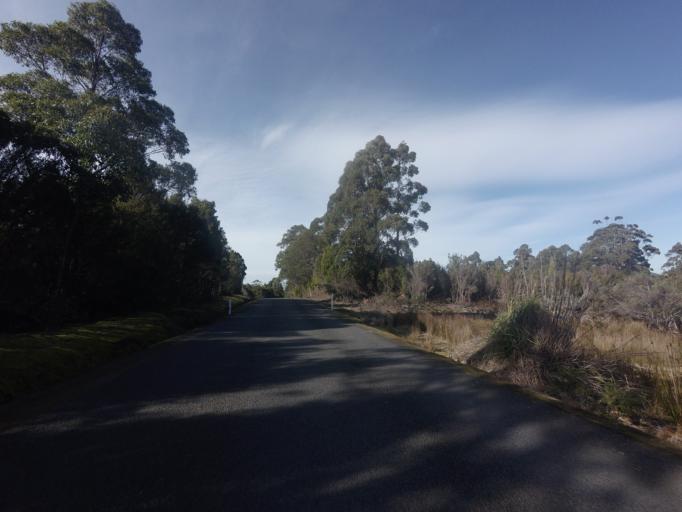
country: AU
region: Tasmania
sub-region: Kingborough
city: Kettering
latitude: -43.1686
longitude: 147.1879
